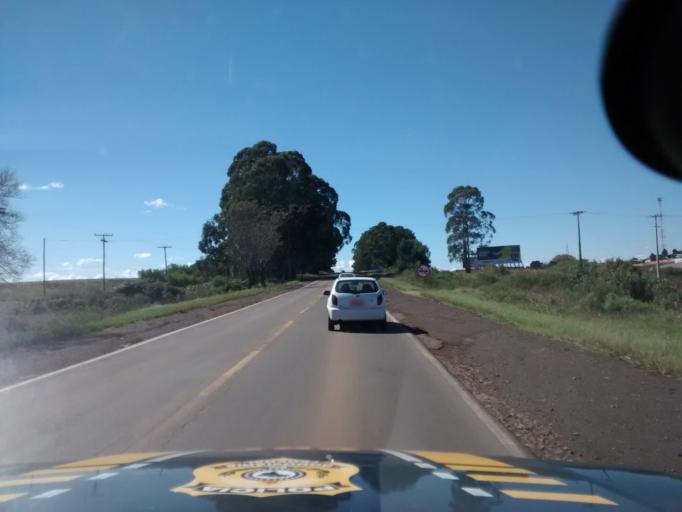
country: BR
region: Rio Grande do Sul
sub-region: Vacaria
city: Vacaria
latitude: -28.4967
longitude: -50.9154
